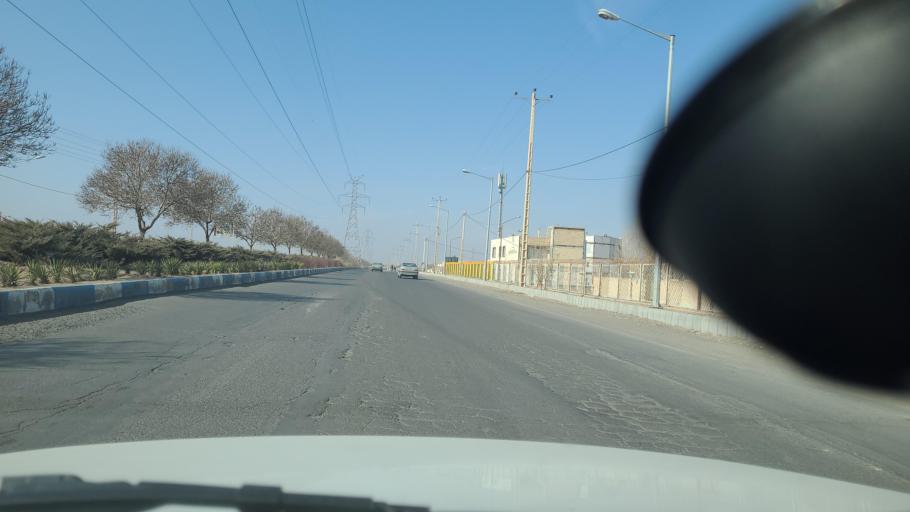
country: IR
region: Razavi Khorasan
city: Fariman
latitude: 35.6954
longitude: 59.8430
